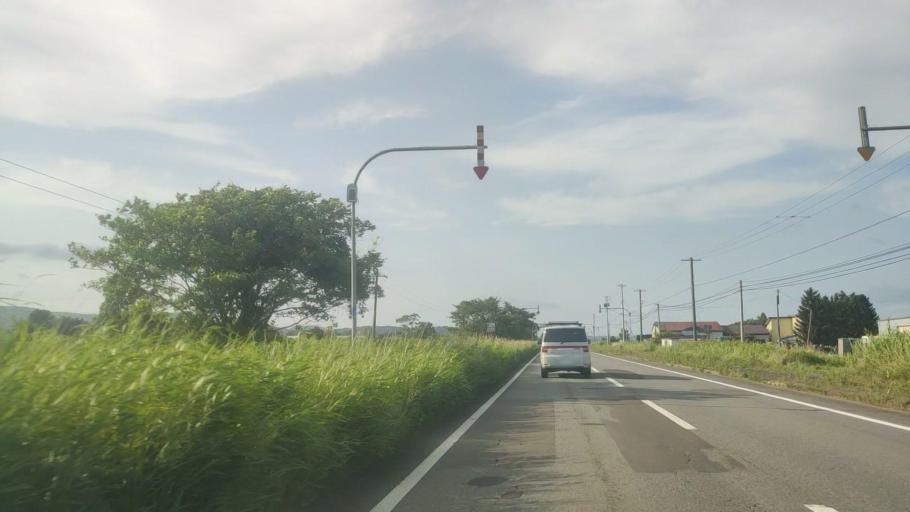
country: JP
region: Hokkaido
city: Chitose
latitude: 42.9578
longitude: 141.7984
